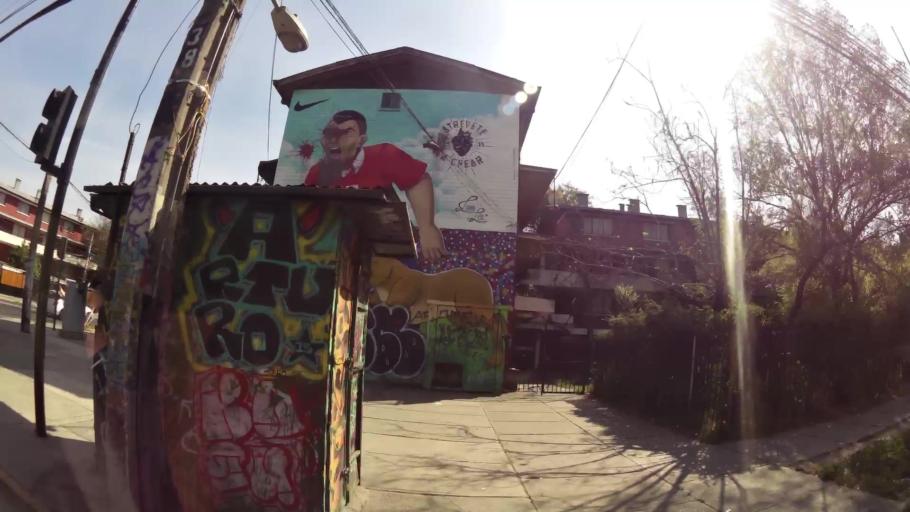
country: CL
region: Santiago Metropolitan
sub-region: Provincia de Santiago
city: Villa Presidente Frei, Nunoa, Santiago, Chile
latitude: -33.4992
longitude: -70.5923
